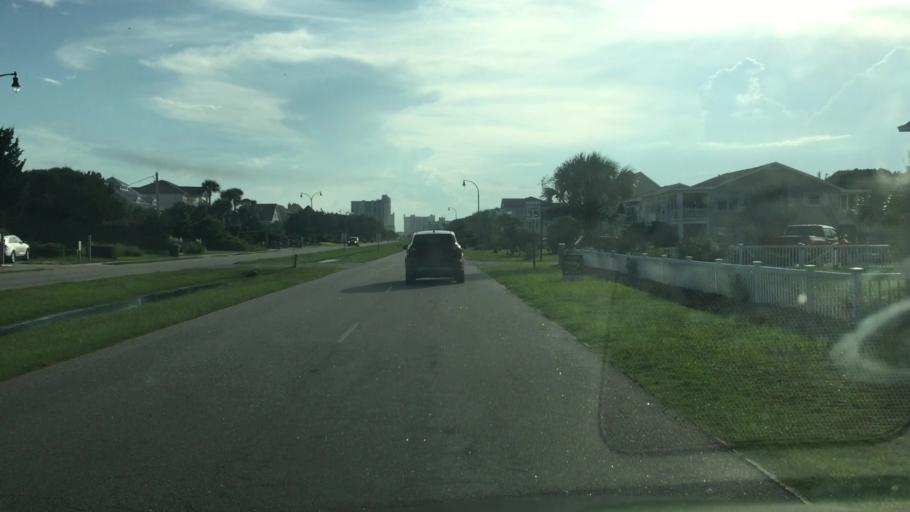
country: US
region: South Carolina
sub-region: Horry County
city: North Myrtle Beach
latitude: 33.8247
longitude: -78.6557
